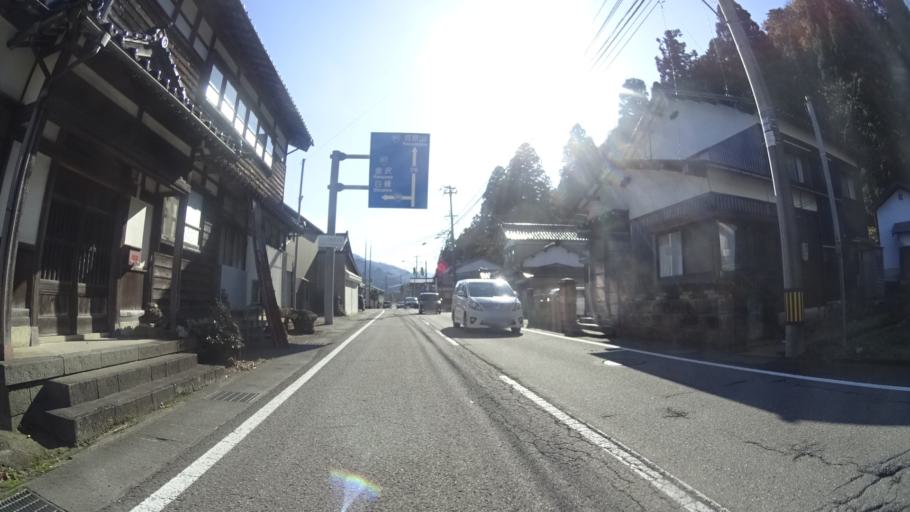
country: JP
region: Ishikawa
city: Tsurugi-asahimachi
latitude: 36.3618
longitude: 136.6124
